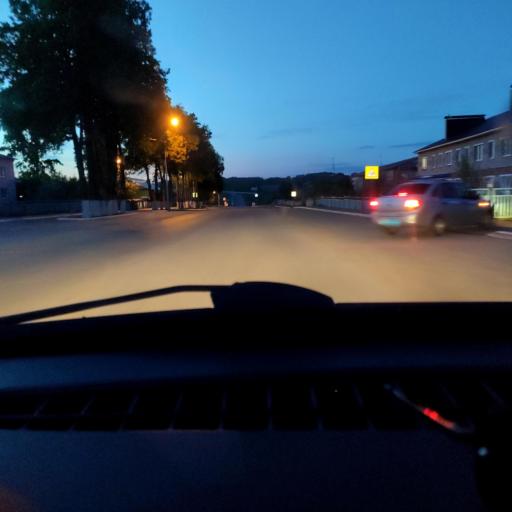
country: RU
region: Bashkortostan
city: Karmaskaly
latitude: 54.3711
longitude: 56.1715
